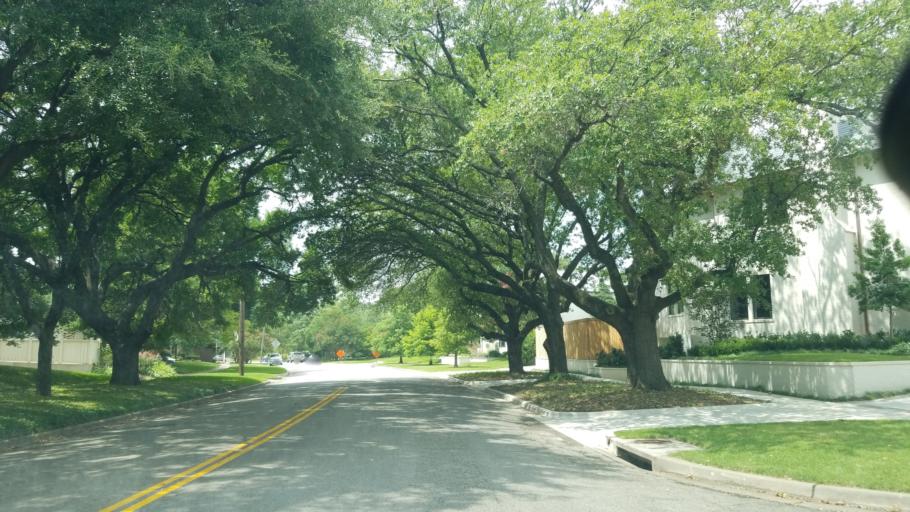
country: US
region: Texas
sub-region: Dallas County
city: University Park
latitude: 32.8415
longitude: -96.8110
